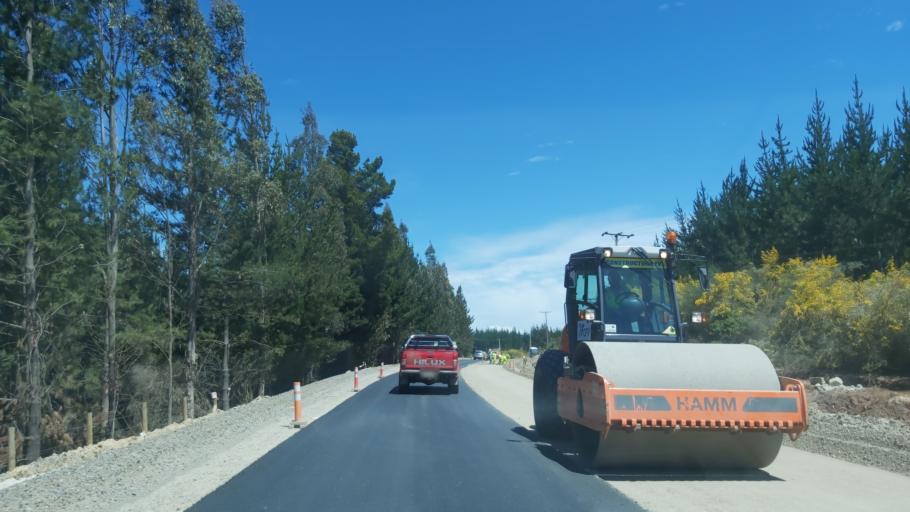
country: CL
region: Maule
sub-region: Provincia de Talca
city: Constitucion
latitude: -35.3810
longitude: -72.4209
